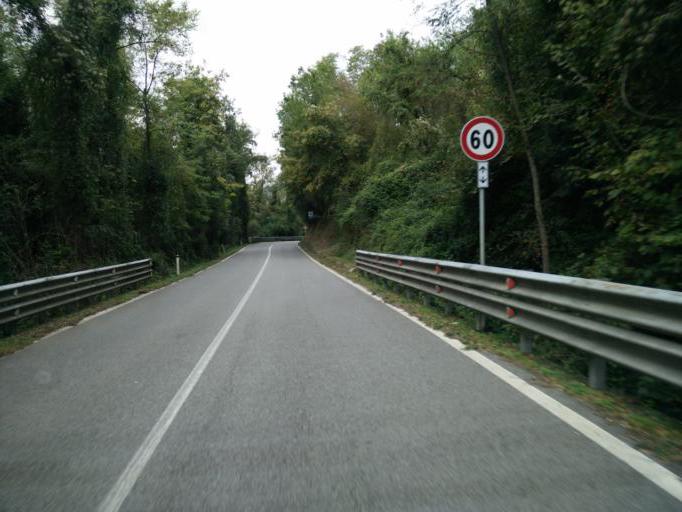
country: IT
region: Tuscany
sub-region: Provincia di Massa-Carrara
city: Fivizzano
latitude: 44.2140
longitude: 10.0923
